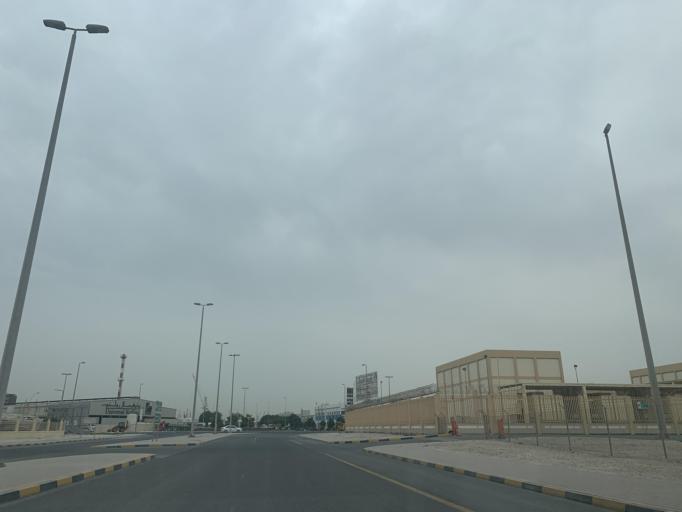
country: BH
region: Muharraq
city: Al Hadd
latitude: 26.2136
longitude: 50.6673
